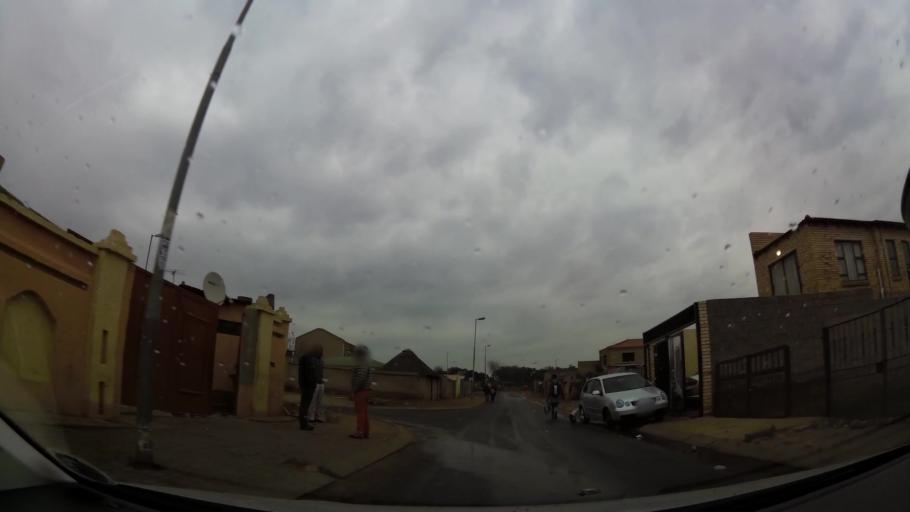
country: ZA
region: Gauteng
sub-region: City of Johannesburg Metropolitan Municipality
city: Soweto
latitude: -26.2471
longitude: 27.8742
